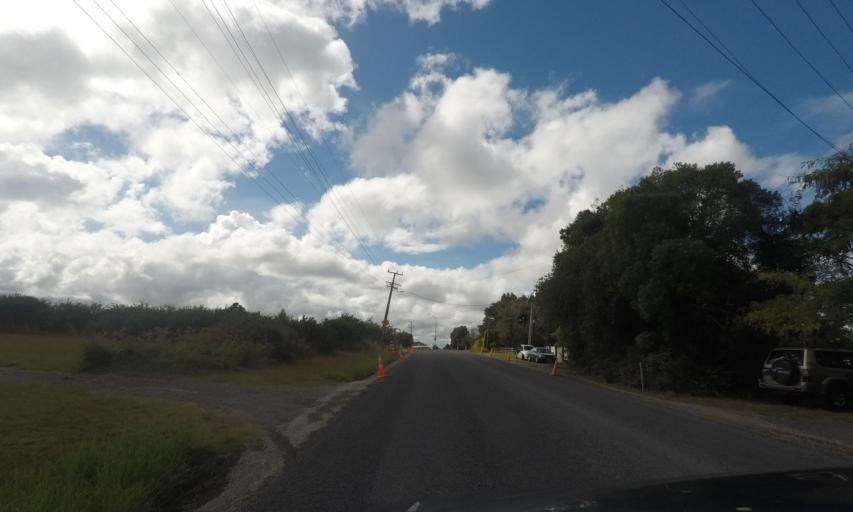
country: NZ
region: Auckland
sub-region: Auckland
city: Rosebank
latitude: -36.7938
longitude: 174.6372
